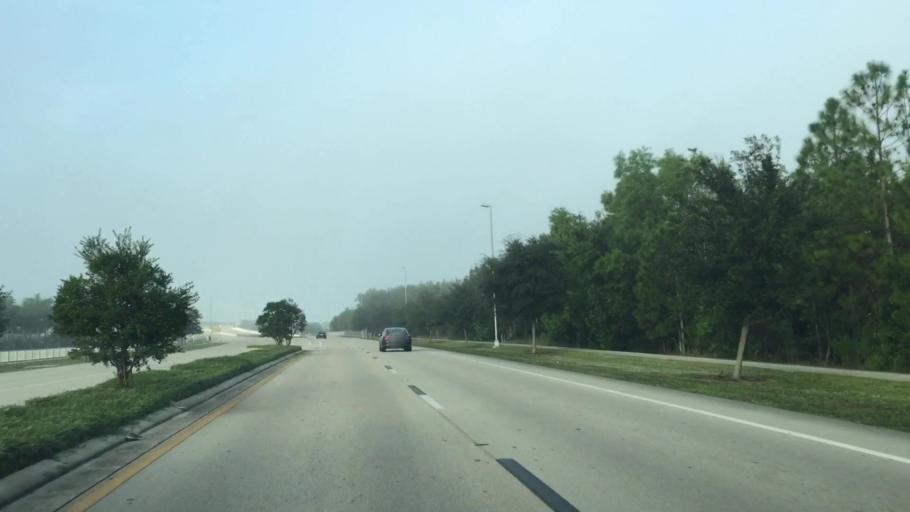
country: US
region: Florida
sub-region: Lee County
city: Three Oaks
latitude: 26.4496
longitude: -81.7757
